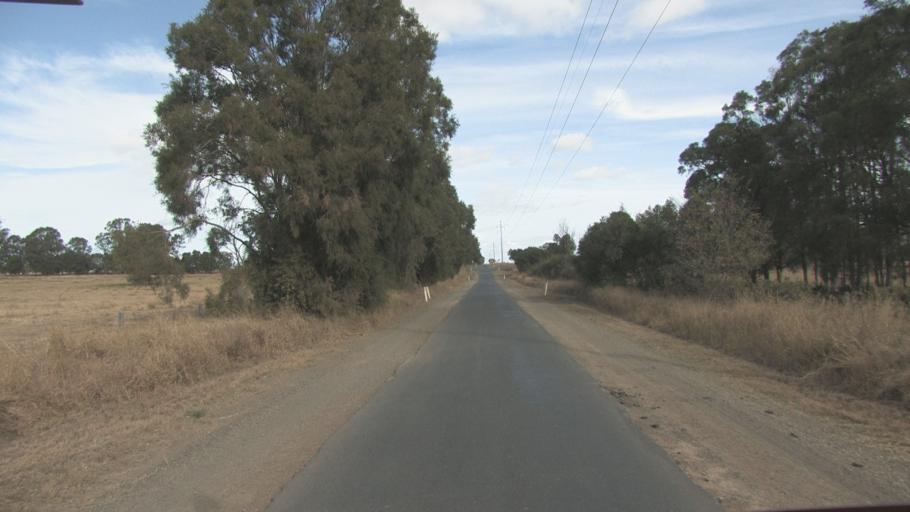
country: AU
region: Queensland
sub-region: Logan
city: Cedar Vale
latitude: -27.9187
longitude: 153.0131
